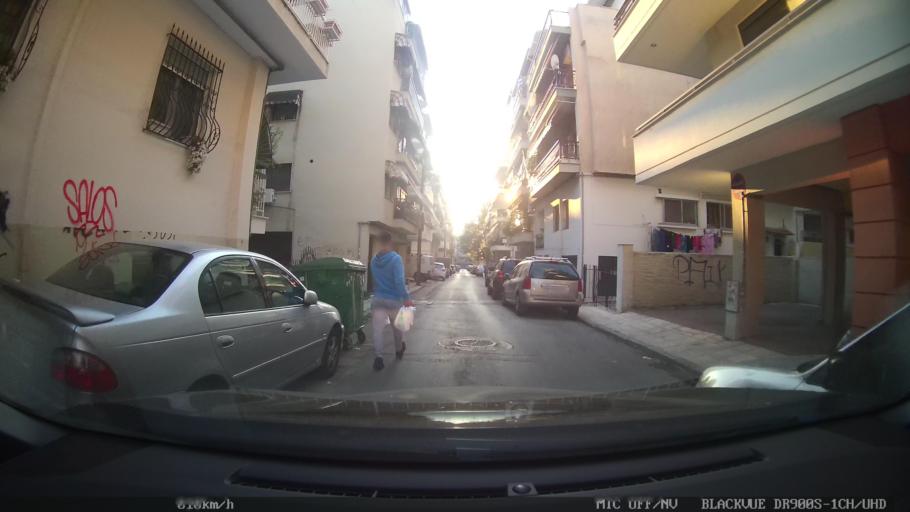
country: GR
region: Central Macedonia
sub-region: Nomos Thessalonikis
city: Triandria
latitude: 40.6030
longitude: 22.9724
